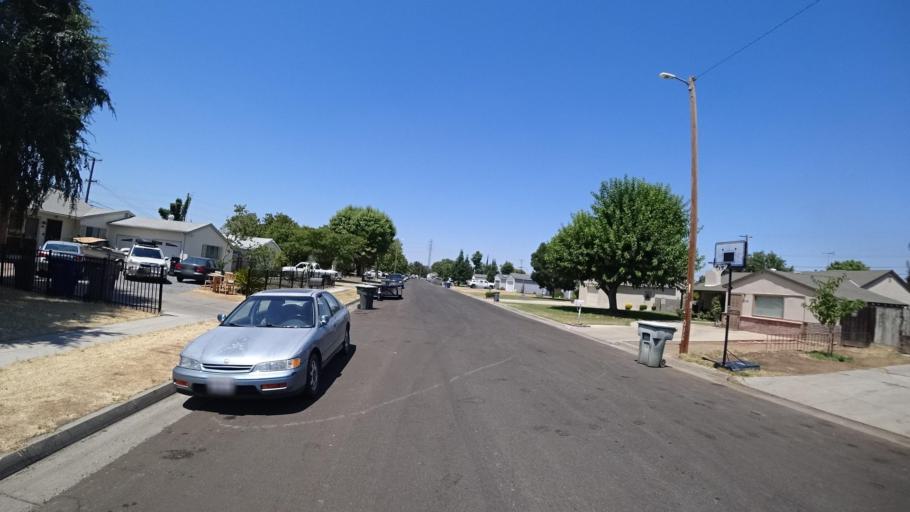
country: US
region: California
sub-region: Fresno County
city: Sunnyside
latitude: 36.7584
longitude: -119.7233
